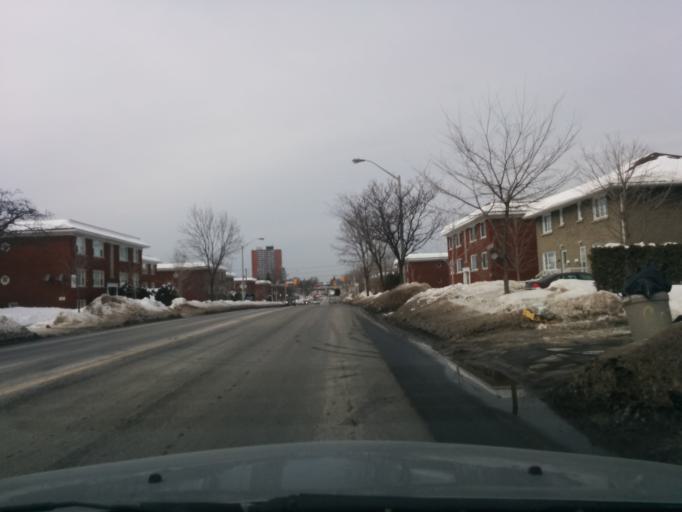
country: CA
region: Ontario
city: Ottawa
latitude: 45.3804
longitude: -75.7376
